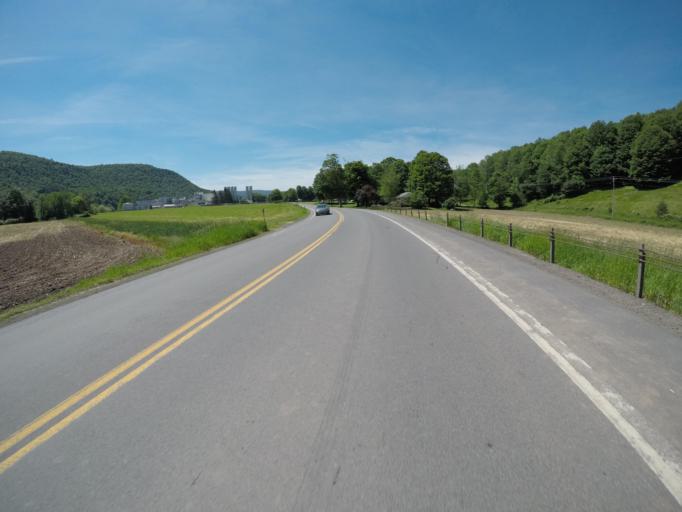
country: US
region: New York
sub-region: Delaware County
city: Delhi
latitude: 42.2492
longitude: -74.9638
